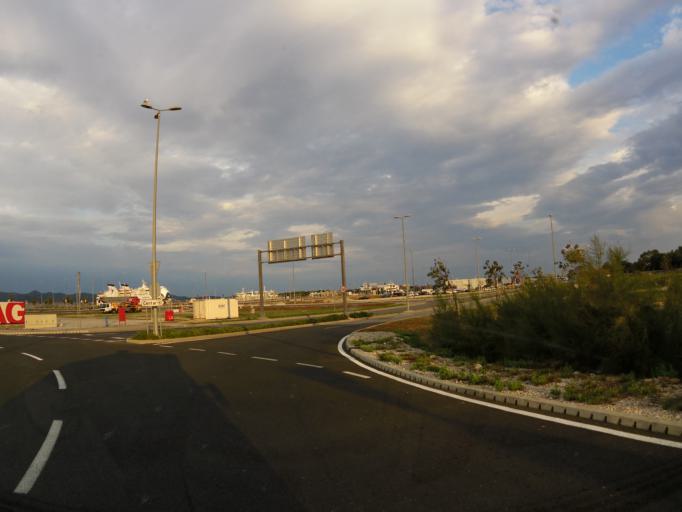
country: HR
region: Zadarska
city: Zadar
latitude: 44.0921
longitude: 15.2629
